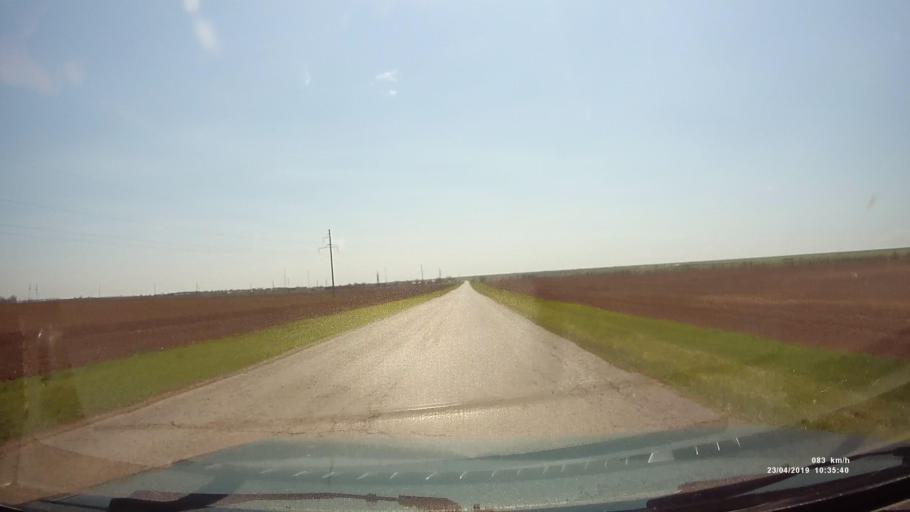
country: RU
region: Kalmykiya
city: Yashalta
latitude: 46.5517
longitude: 42.6271
